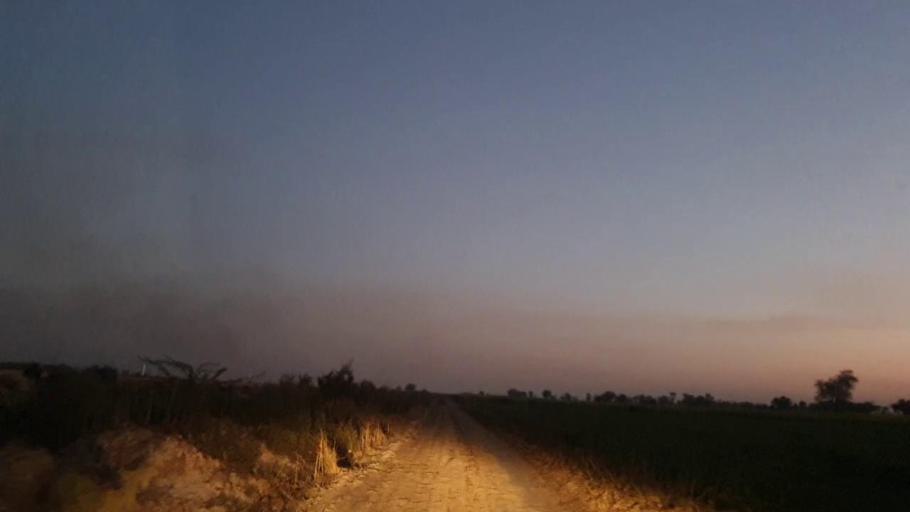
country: PK
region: Sindh
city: Nawabshah
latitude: 26.3328
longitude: 68.3743
